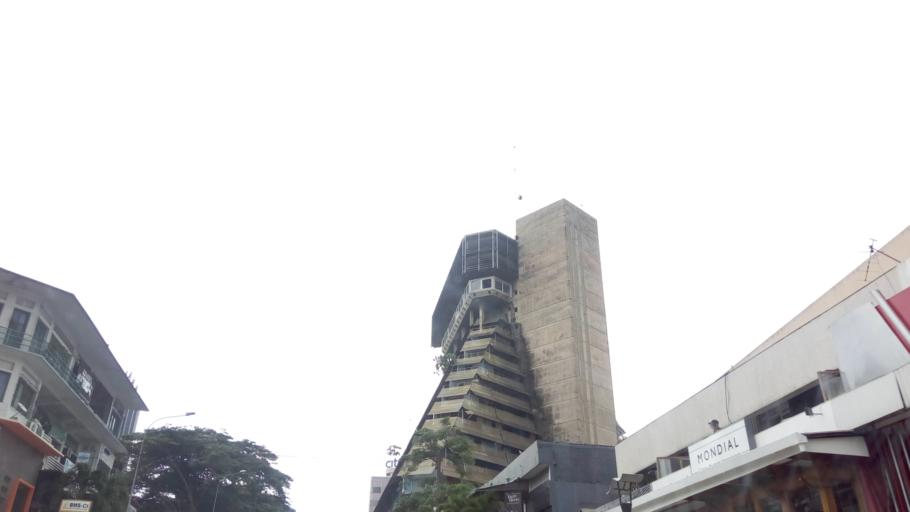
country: CI
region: Lagunes
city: Abidjan
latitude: 5.3235
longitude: -4.0167
